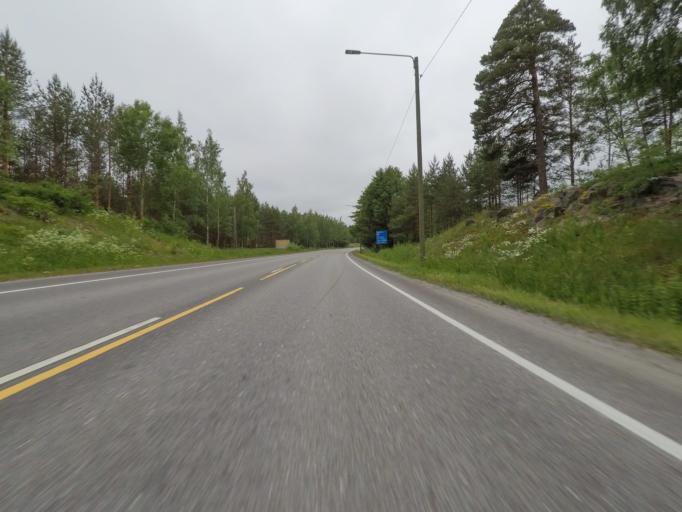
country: FI
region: Varsinais-Suomi
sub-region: Turku
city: Naantali
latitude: 60.4697
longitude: 22.0809
